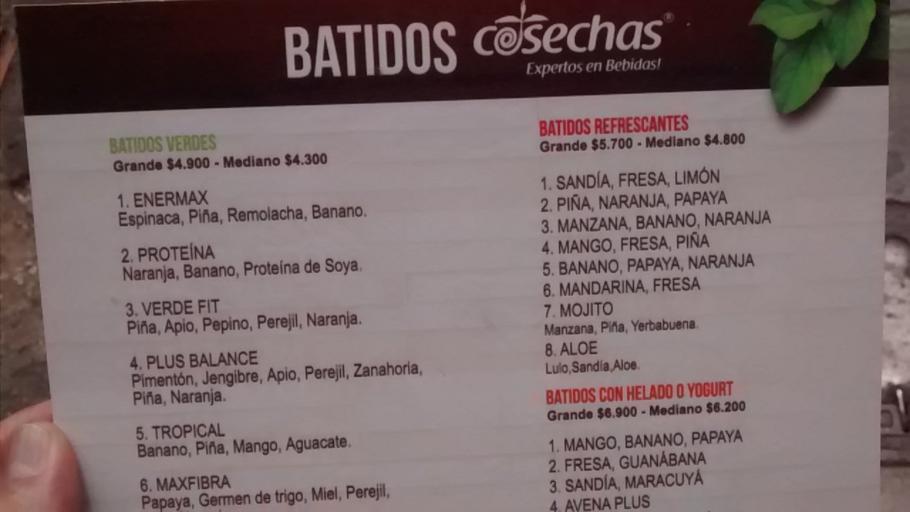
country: CO
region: Bogota D.C.
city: Bogota
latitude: 4.6079
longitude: -74.0705
